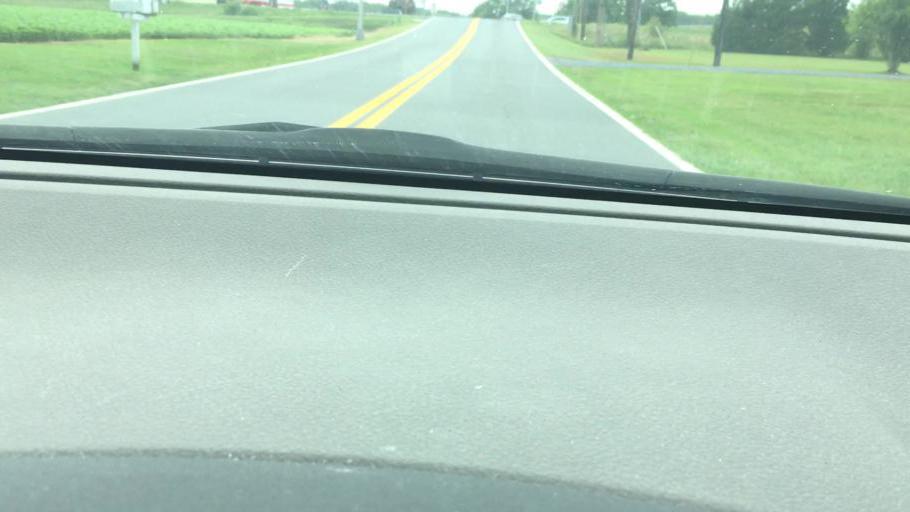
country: US
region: Maryland
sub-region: Worcester County
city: Pocomoke City
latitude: 38.0616
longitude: -75.5440
